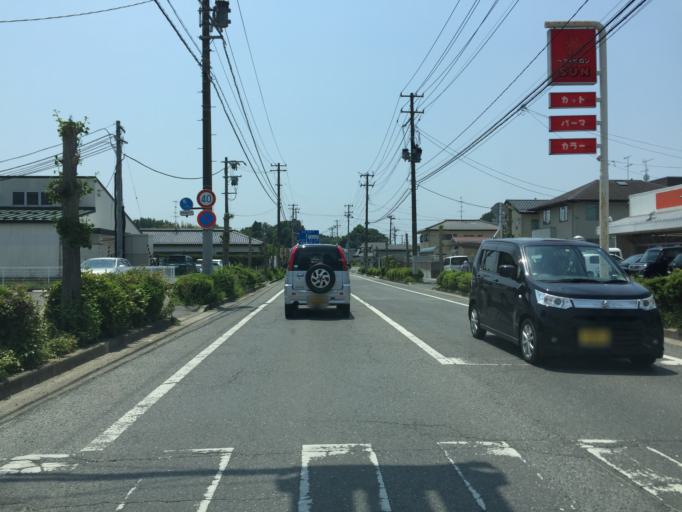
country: JP
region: Miyagi
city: Marumori
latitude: 37.8038
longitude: 140.9126
